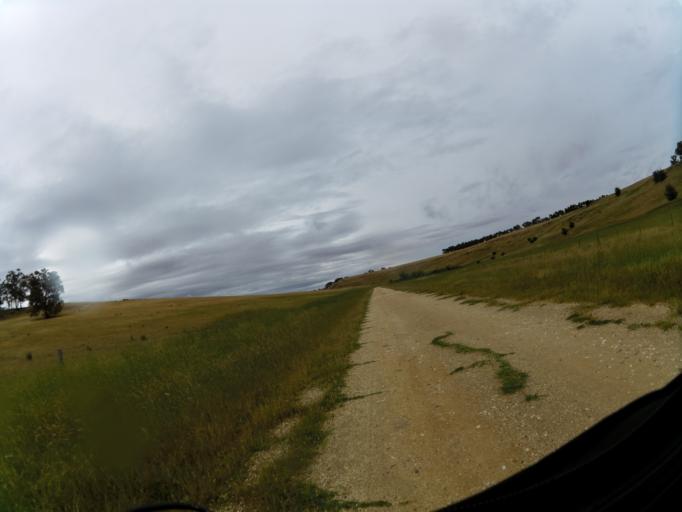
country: AU
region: Victoria
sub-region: Mount Alexander
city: Castlemaine
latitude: -37.2076
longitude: 144.0249
